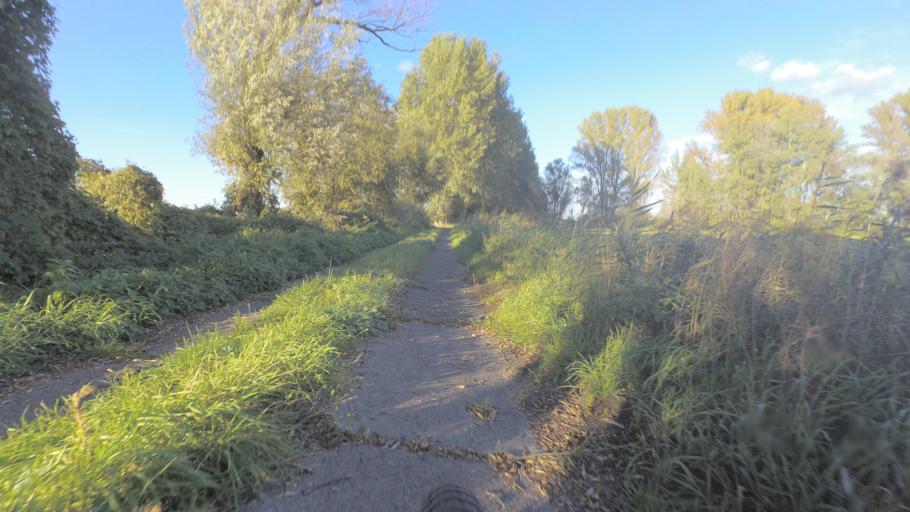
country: DE
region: Brandenburg
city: Rangsdorf
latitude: 52.2908
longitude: 13.3458
